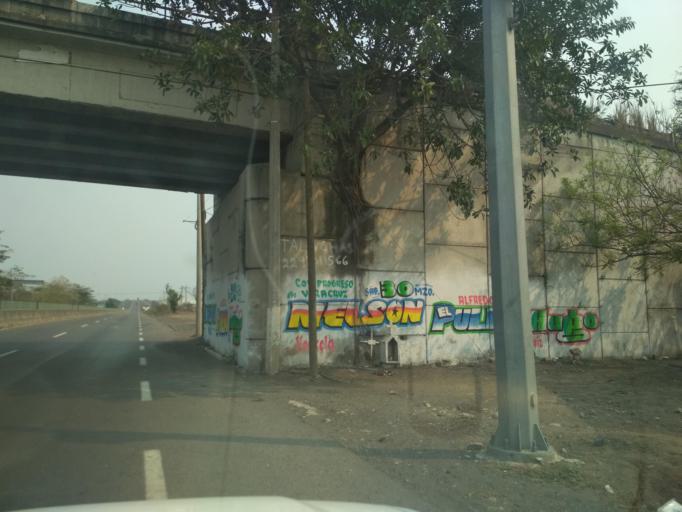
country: MX
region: Veracruz
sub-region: Veracruz
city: Delfino Victoria (Santa Fe)
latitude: 19.1743
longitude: -96.2688
